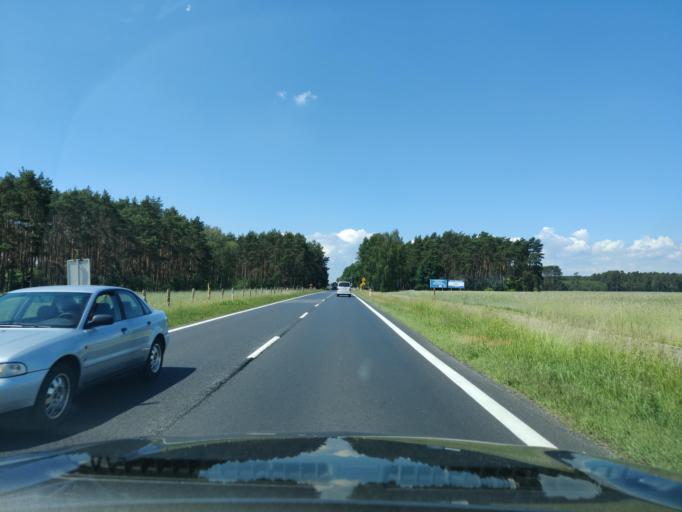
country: PL
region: Greater Poland Voivodeship
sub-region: Powiat wolsztynski
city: Wolsztyn
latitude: 52.1314
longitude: 16.1829
